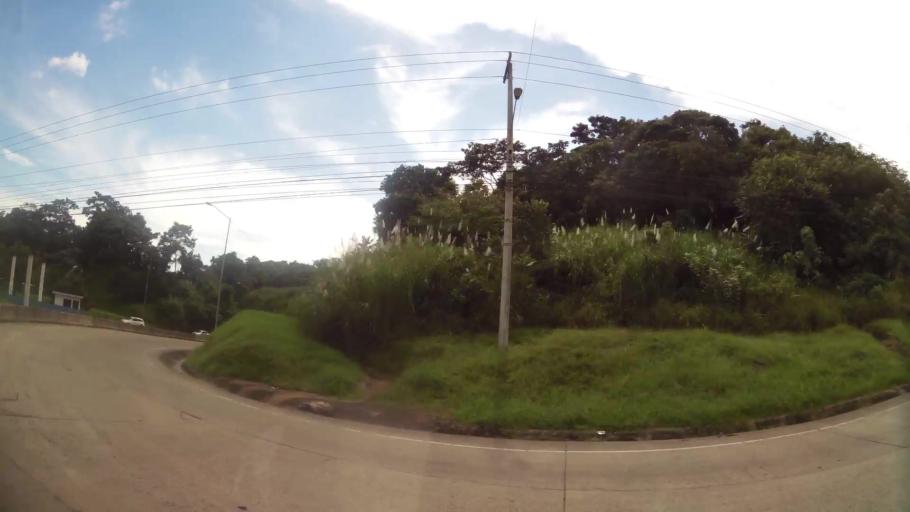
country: PA
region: Panama
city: Panama
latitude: 9.0342
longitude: -79.5377
